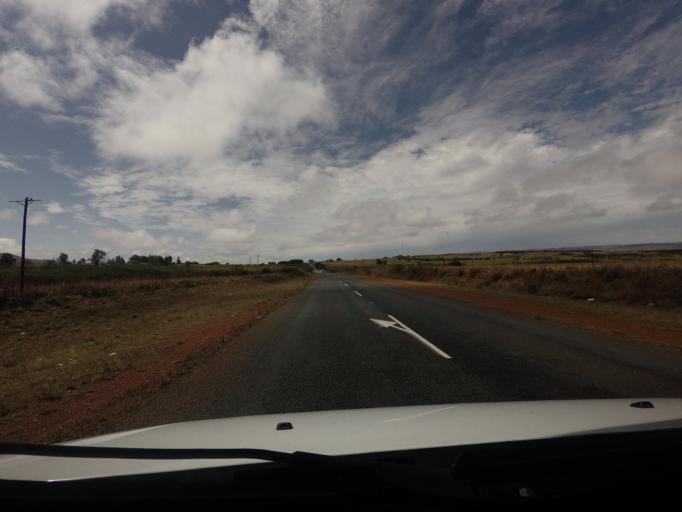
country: ZA
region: Mpumalanga
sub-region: Ehlanzeni District
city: Lydenburg
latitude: -25.1753
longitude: 30.3697
